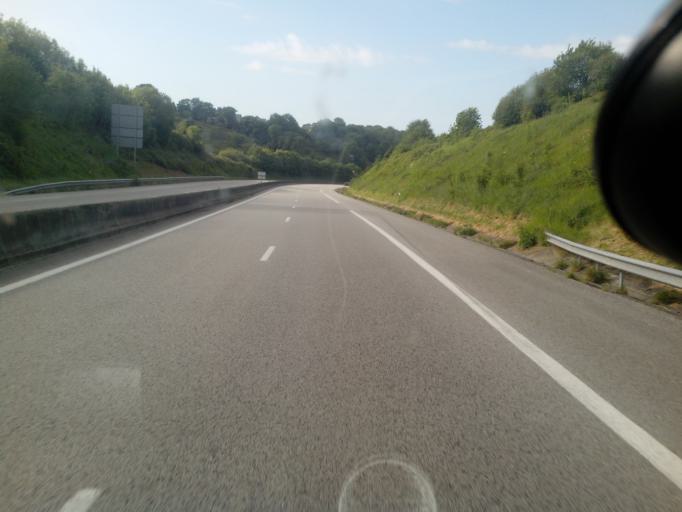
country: FR
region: Lower Normandy
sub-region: Departement du Calvados
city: La Riviere-Saint-Sauveur
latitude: 49.3974
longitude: 0.2620
